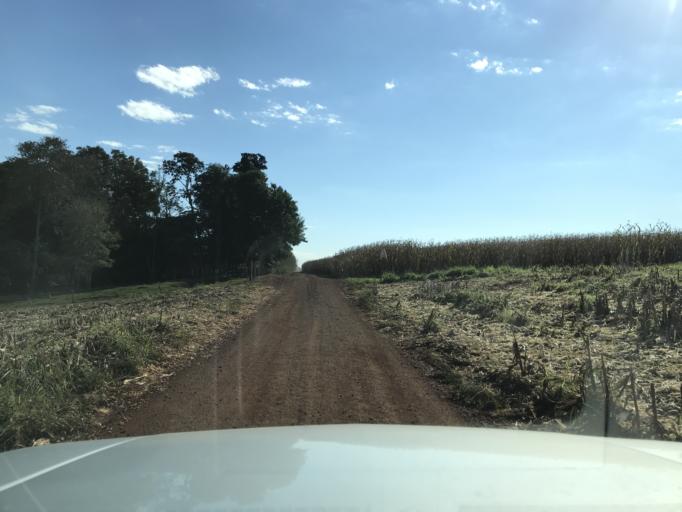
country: BR
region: Parana
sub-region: Palotina
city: Palotina
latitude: -24.2694
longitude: -53.8149
